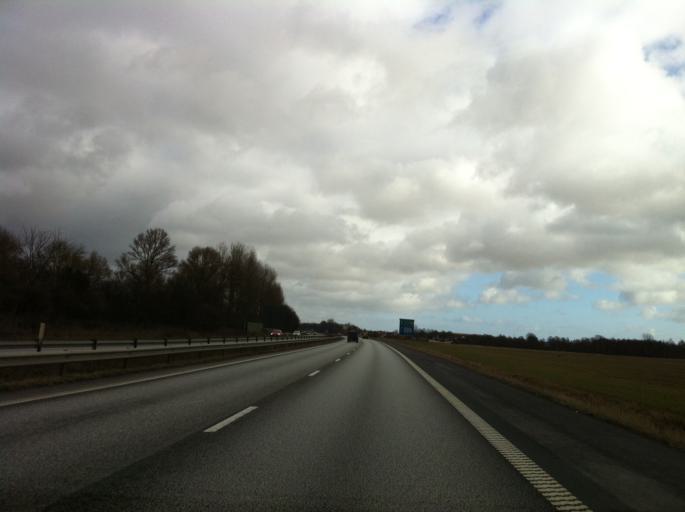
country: SE
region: Skane
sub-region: Kristianstads Kommun
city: Kristianstad
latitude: 56.0211
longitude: 14.1076
